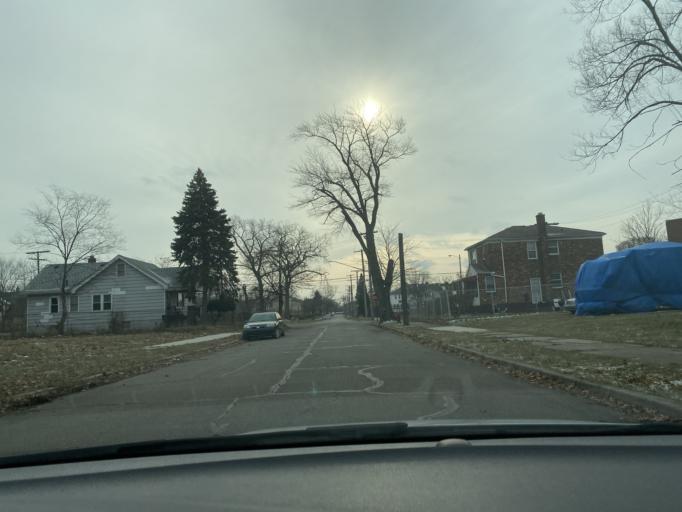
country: US
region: Michigan
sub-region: Wayne County
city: Highland Park
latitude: 42.3691
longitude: -83.1308
